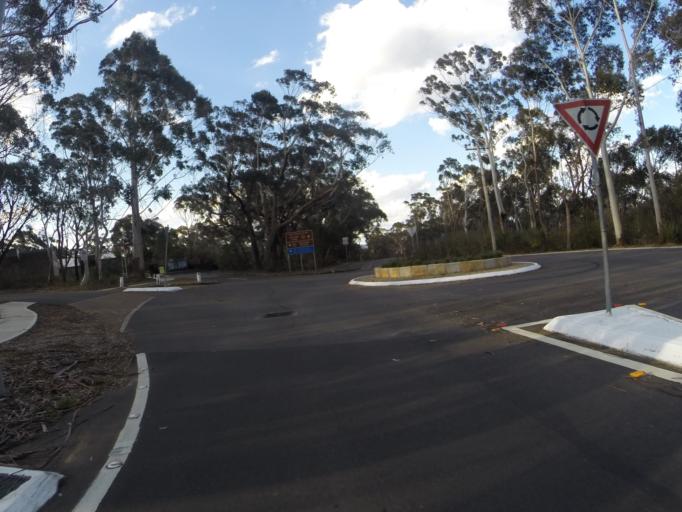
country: AU
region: New South Wales
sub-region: Blue Mountains Municipality
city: Blackheath
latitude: -33.6313
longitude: 150.3066
